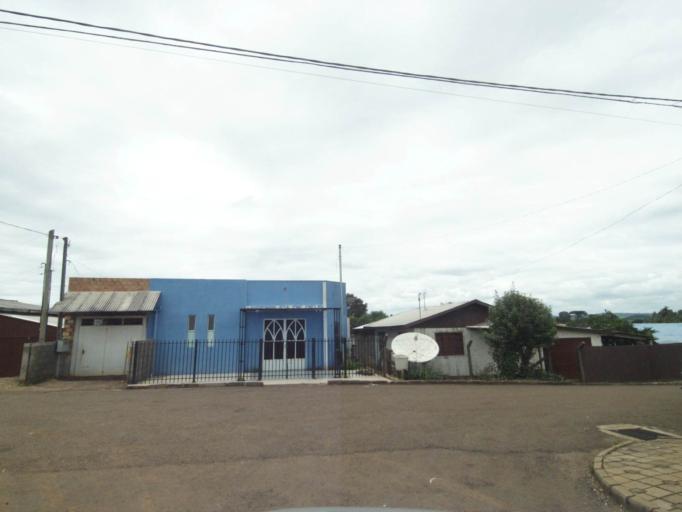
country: BR
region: Rio Grande do Sul
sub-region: Lagoa Vermelha
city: Lagoa Vermelha
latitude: -28.2147
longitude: -51.5388
